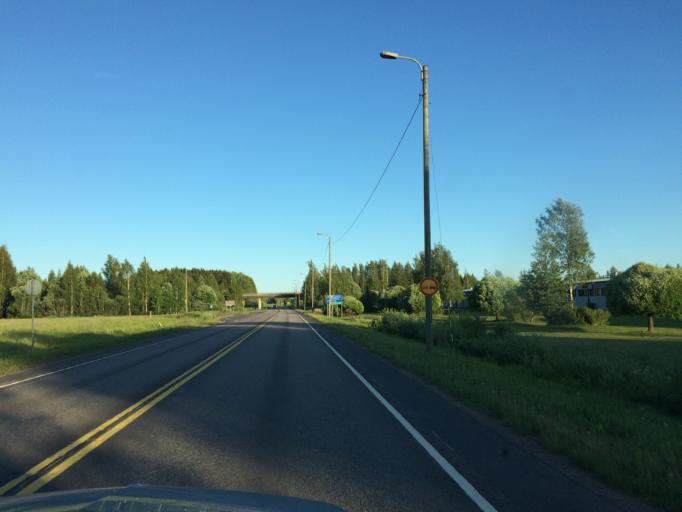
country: FI
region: Haeme
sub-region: Haemeenlinna
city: Tervakoski
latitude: 60.8203
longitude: 24.6380
